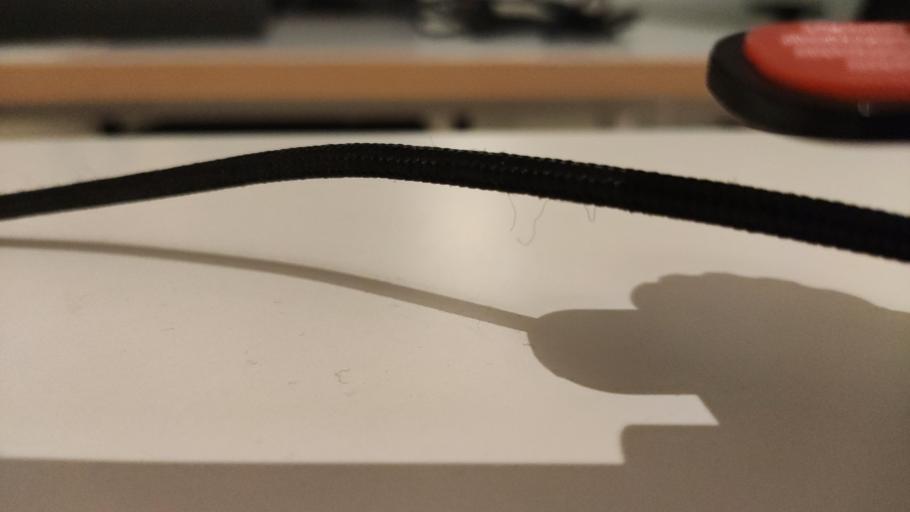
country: RU
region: Moskovskaya
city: Kurovskoye
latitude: 55.5998
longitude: 38.9253
